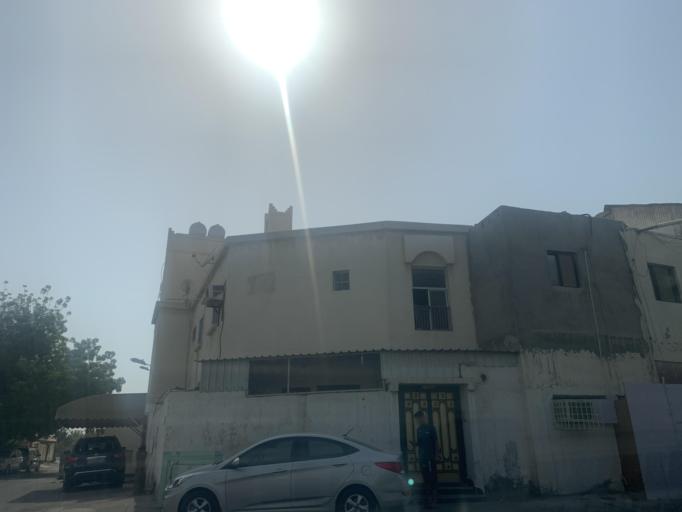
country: BH
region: Manama
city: Jidd Hafs
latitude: 26.2120
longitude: 50.4658
